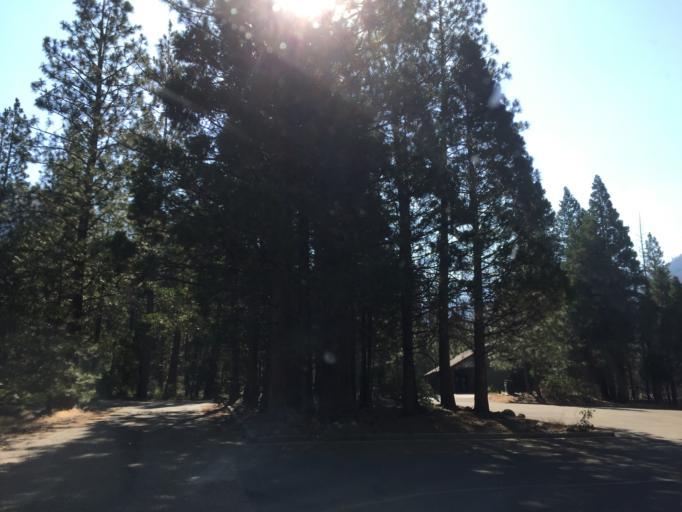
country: US
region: California
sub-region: Tulare County
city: Three Rivers
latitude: 36.7908
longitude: -118.6684
